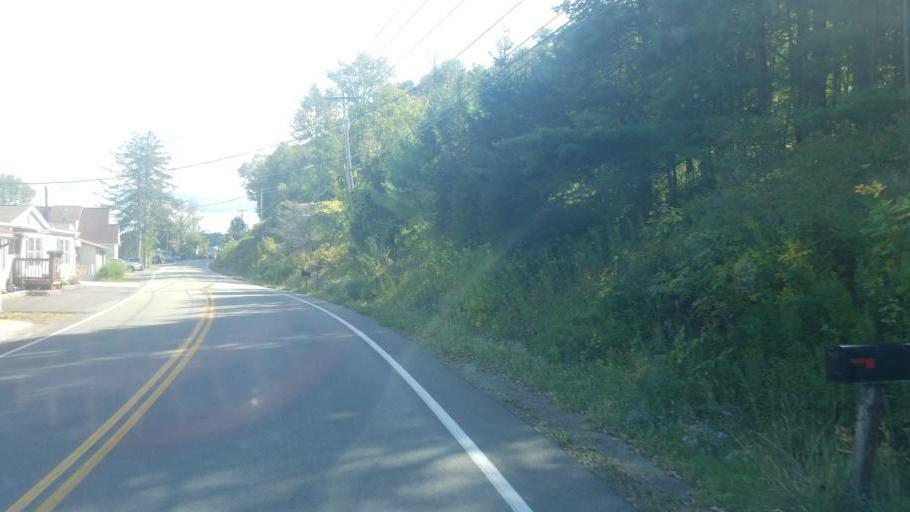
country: US
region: New York
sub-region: Allegany County
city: Cuba
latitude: 42.2478
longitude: -78.2910
